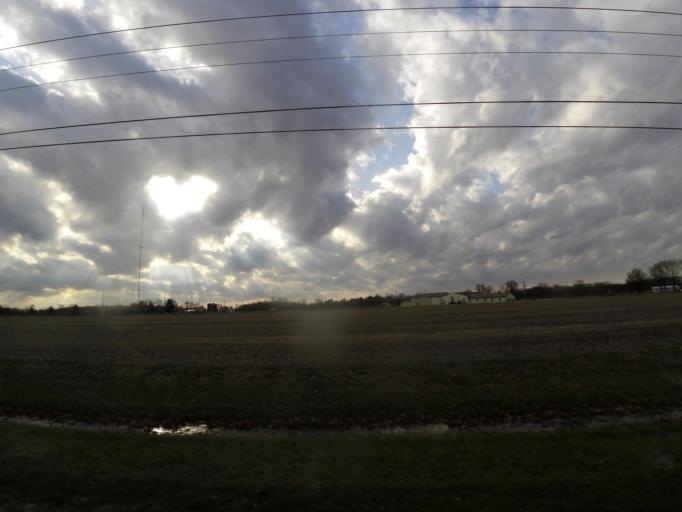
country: US
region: Illinois
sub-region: Fayette County
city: Ramsey
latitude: 39.1386
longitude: -89.1037
